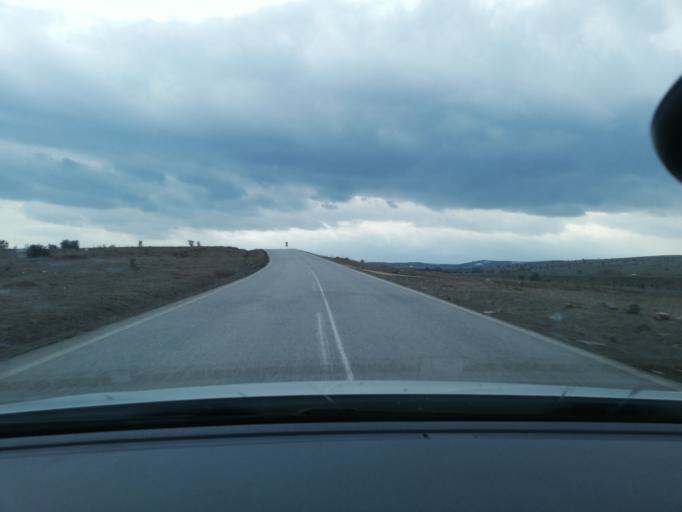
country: TR
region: Bolu
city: Gerede
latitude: 40.7124
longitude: 32.2251
